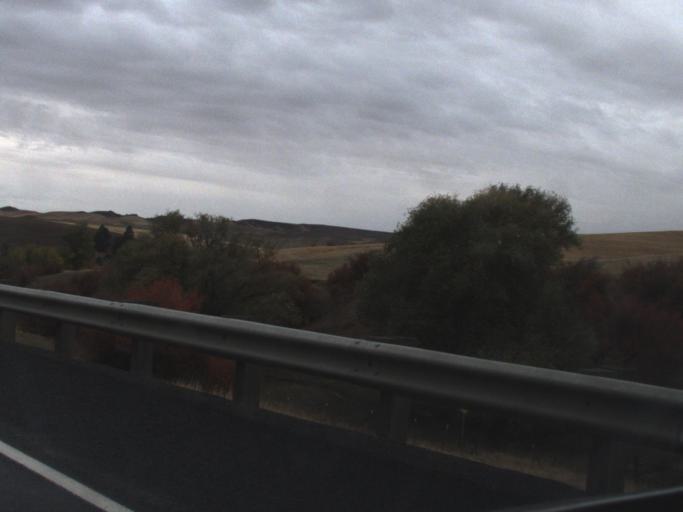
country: US
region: Washington
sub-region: Whitman County
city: Pullman
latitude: 46.5989
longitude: -117.1714
